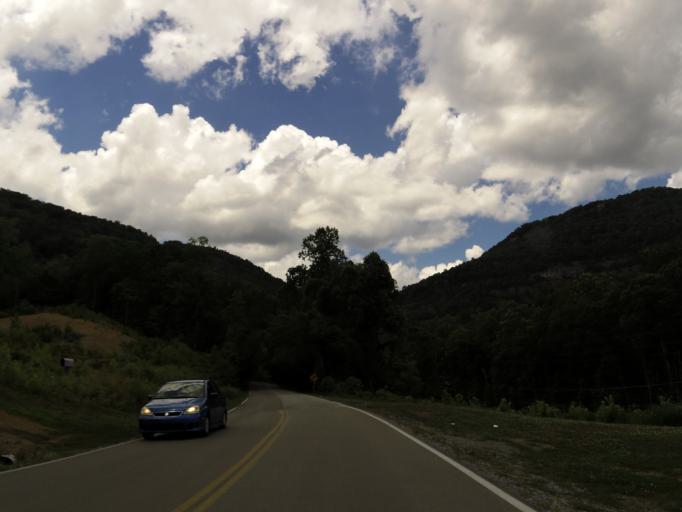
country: US
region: Tennessee
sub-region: Claiborne County
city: Harrogate
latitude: 36.5952
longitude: -83.6676
